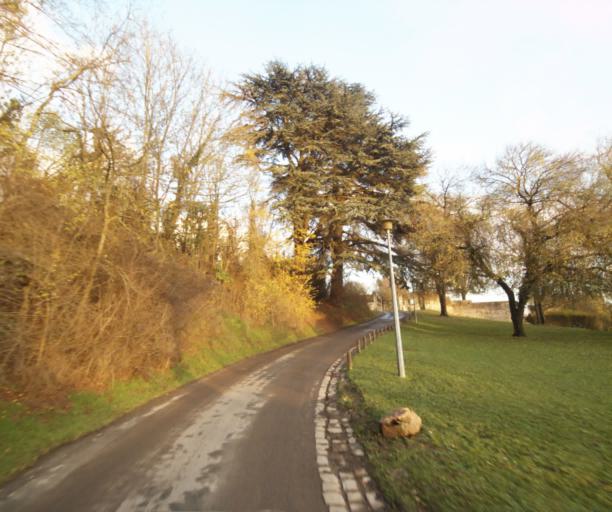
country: FR
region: Ile-de-France
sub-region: Departement des Yvelines
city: Meulan-en-Yvelines
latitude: 49.0082
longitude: 1.9190
